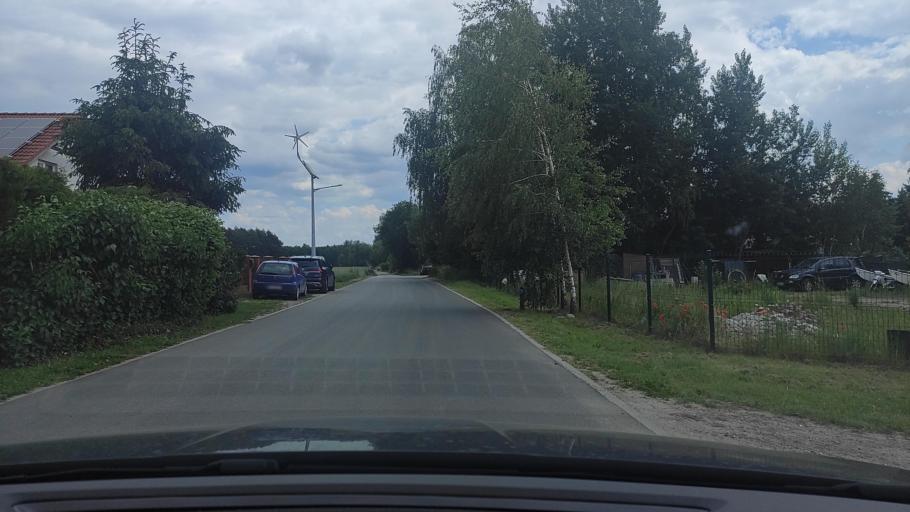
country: PL
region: Greater Poland Voivodeship
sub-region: Powiat poznanski
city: Pobiedziska
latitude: 52.4951
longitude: 17.1880
